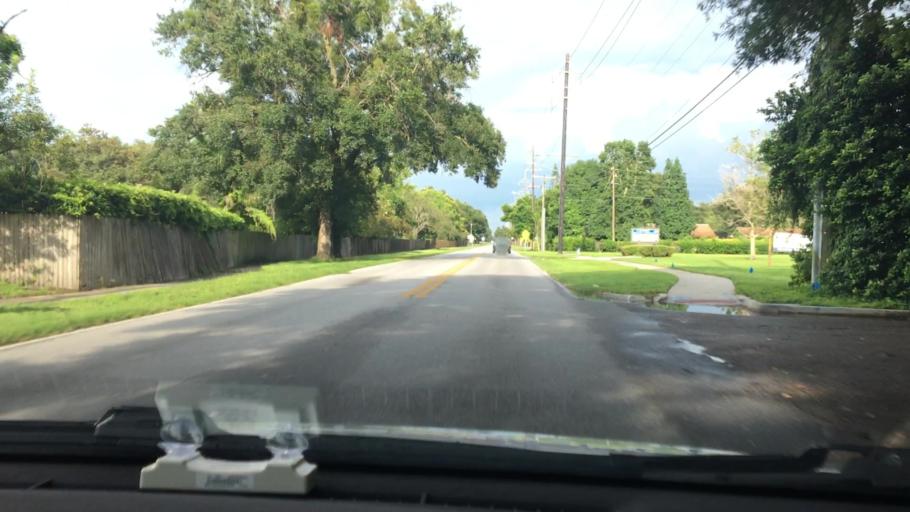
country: US
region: Florida
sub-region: Orange County
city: Conway
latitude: 28.5060
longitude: -81.3290
